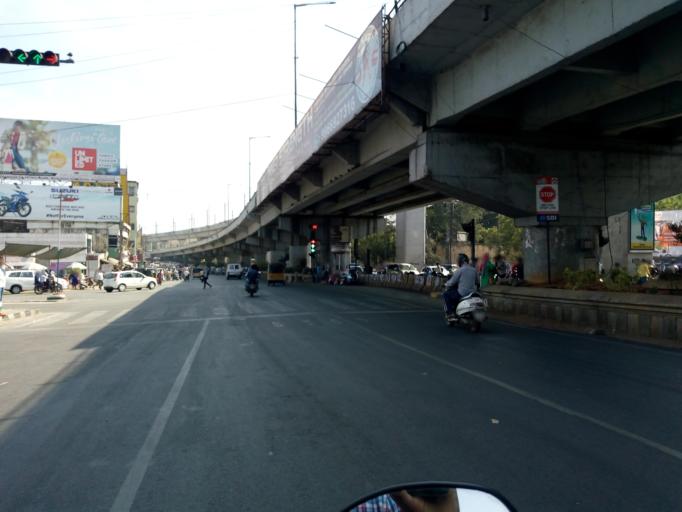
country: IN
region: Telangana
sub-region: Hyderabad
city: Malkajgiri
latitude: 17.4271
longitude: 78.5308
